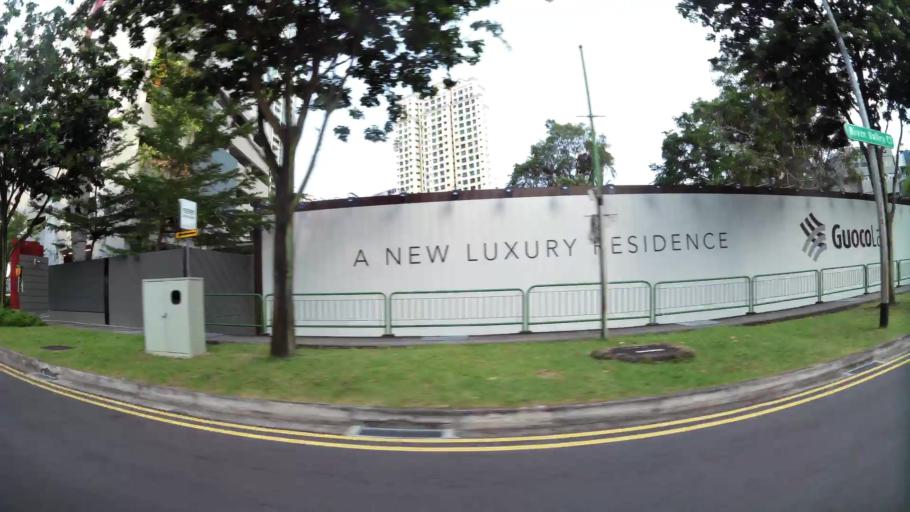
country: SG
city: Singapore
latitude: 1.2934
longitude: 103.8371
